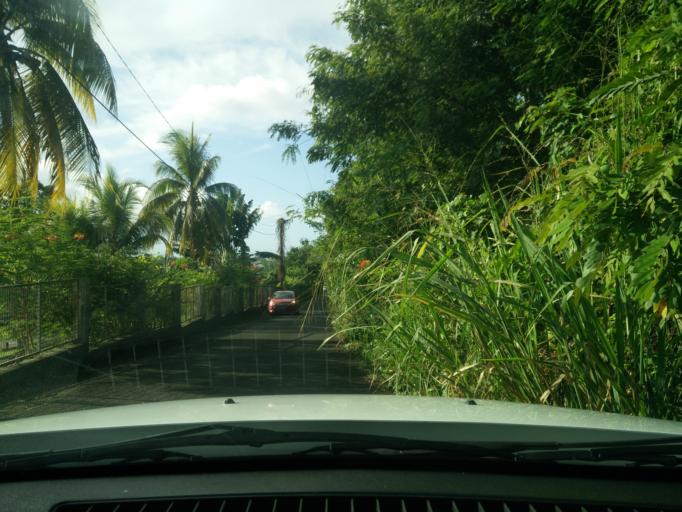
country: GP
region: Guadeloupe
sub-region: Guadeloupe
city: Baie-Mahault
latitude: 16.2535
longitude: -61.5846
